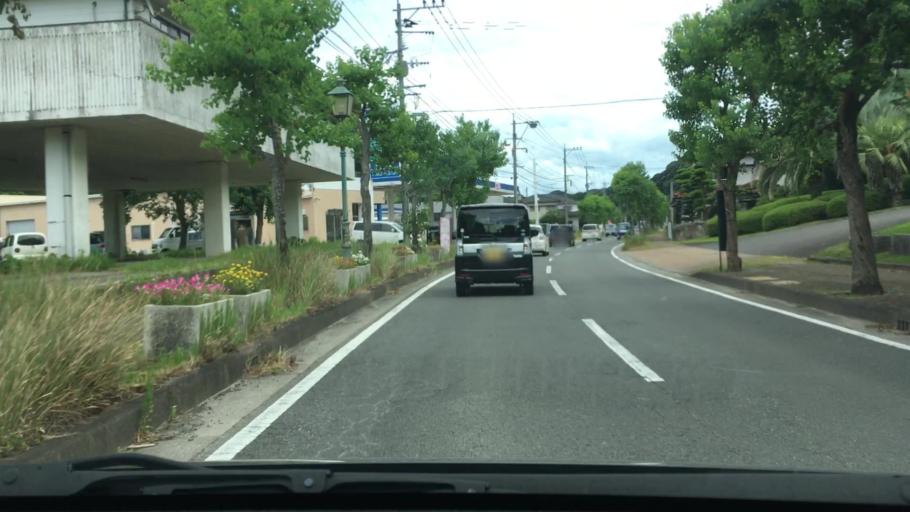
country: JP
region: Nagasaki
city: Sasebo
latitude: 32.9906
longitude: 129.7646
